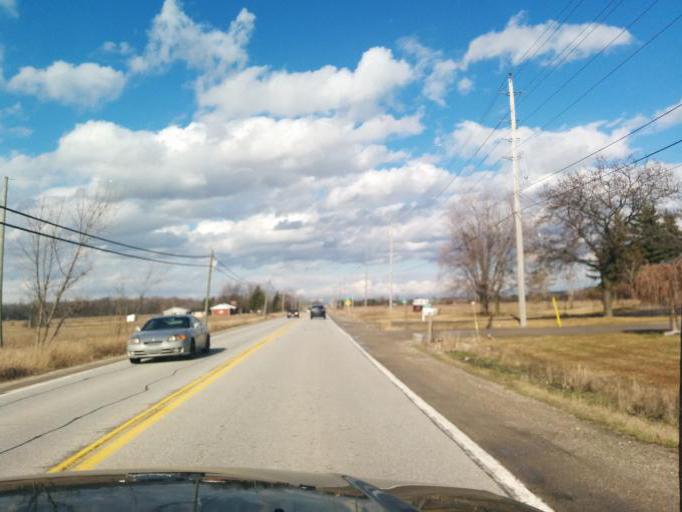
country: CA
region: Ontario
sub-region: Halton
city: Milton
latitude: 43.5225
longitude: -79.7956
